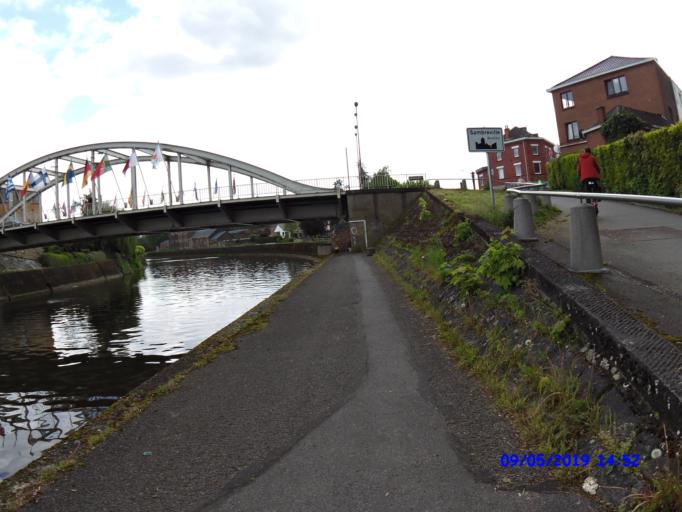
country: BE
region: Wallonia
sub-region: Province de Namur
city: La Bruyere
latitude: 50.4518
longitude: 4.6336
